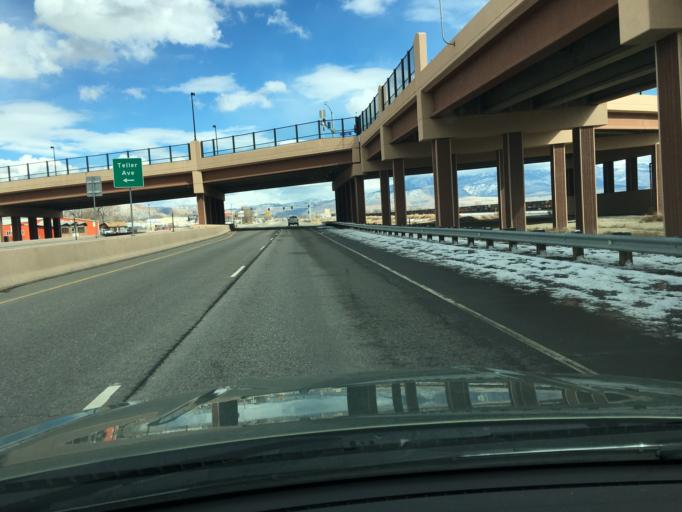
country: US
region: Colorado
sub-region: Mesa County
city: Fruitvale
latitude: 39.0726
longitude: -108.5161
